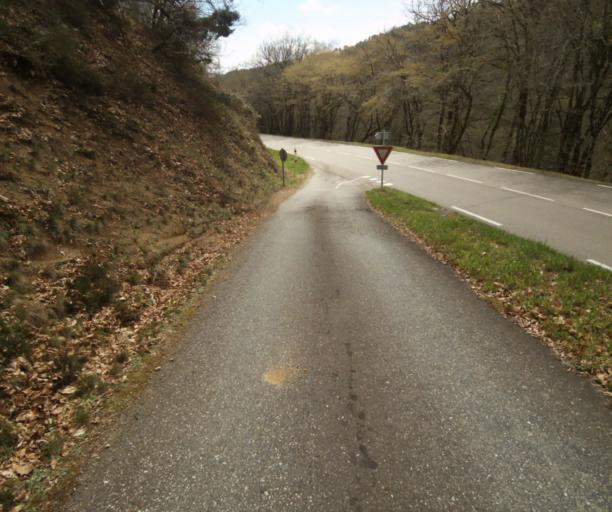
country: FR
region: Limousin
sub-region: Departement de la Correze
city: Sainte-Fortunade
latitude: 45.1828
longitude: 1.8484
